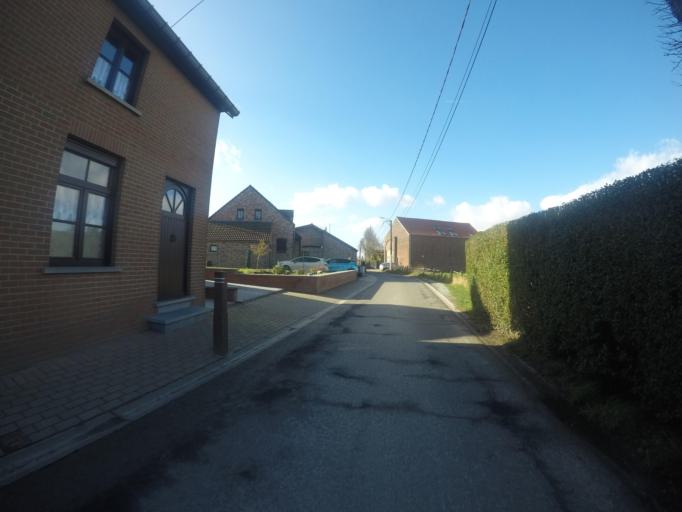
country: BE
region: Wallonia
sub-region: Province du Brabant Wallon
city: Rebecq-Rognon
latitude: 50.6801
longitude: 4.1500
